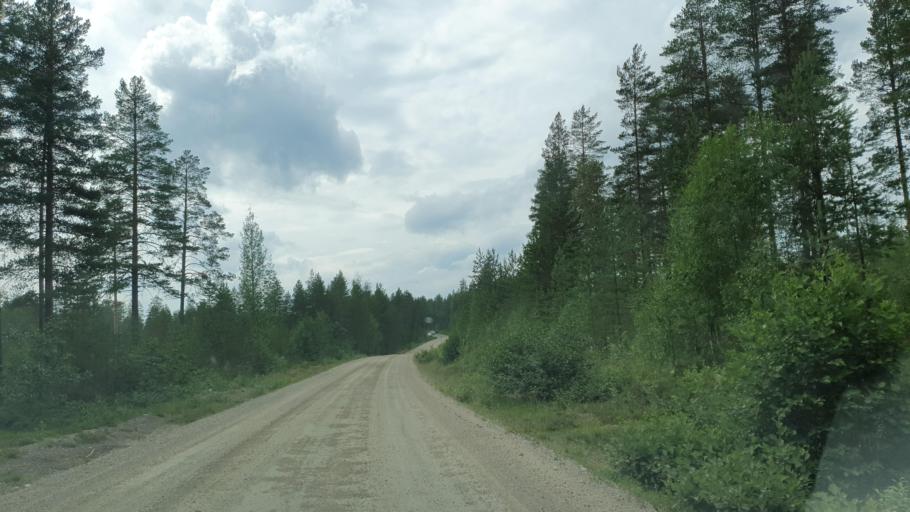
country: FI
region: Kainuu
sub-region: Kehys-Kainuu
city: Kuhmo
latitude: 64.7262
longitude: 29.7090
